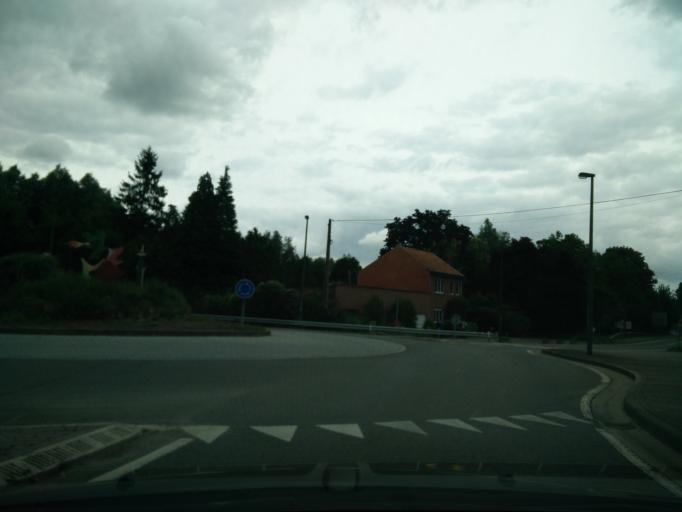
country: BE
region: Wallonia
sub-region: Province de Liege
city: Bassenge
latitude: 50.7781
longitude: 5.6593
